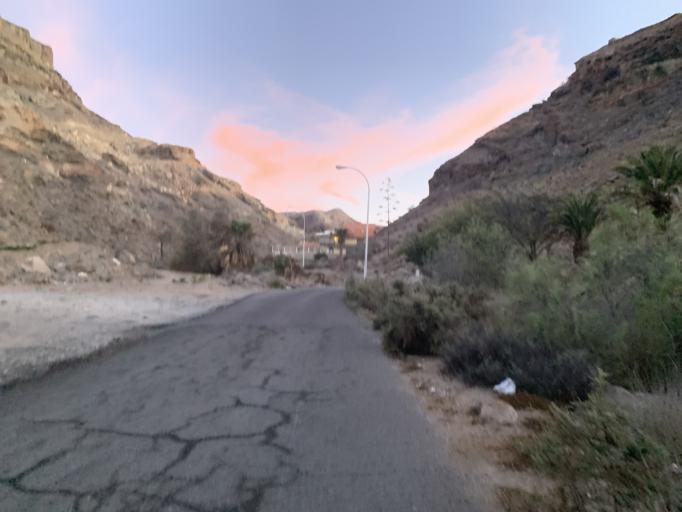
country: ES
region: Canary Islands
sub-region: Provincia de Las Palmas
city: Puerto Rico
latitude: 27.8038
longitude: -15.7319
